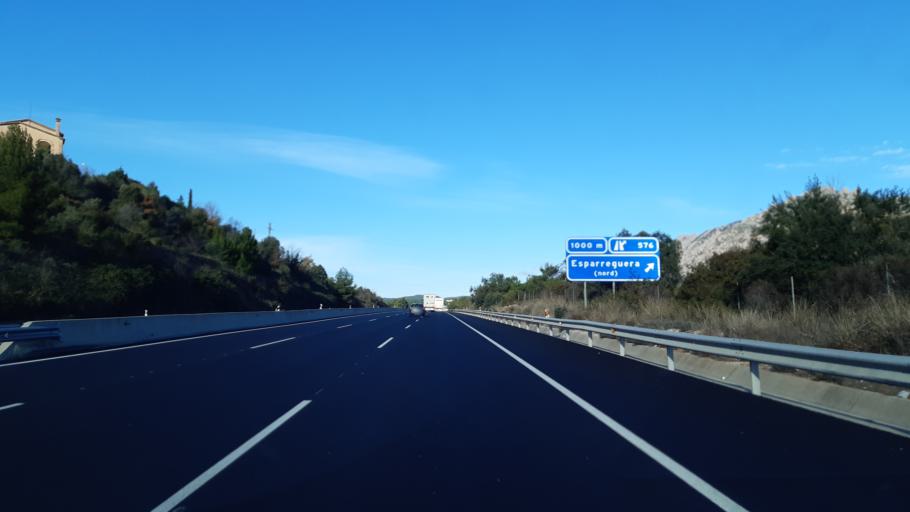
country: ES
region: Catalonia
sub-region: Provincia de Barcelona
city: Esparreguera
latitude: 41.5484
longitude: 1.8500
